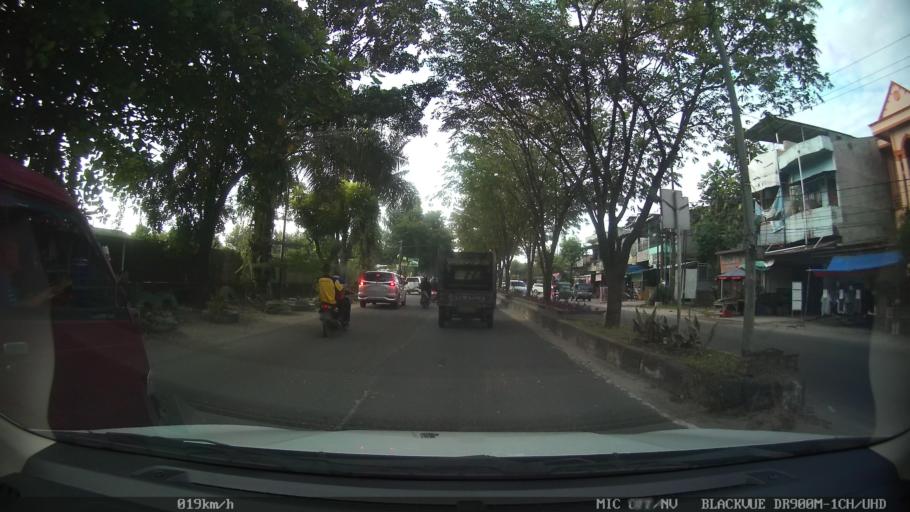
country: ID
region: North Sumatra
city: Sunggal
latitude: 3.5621
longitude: 98.6163
